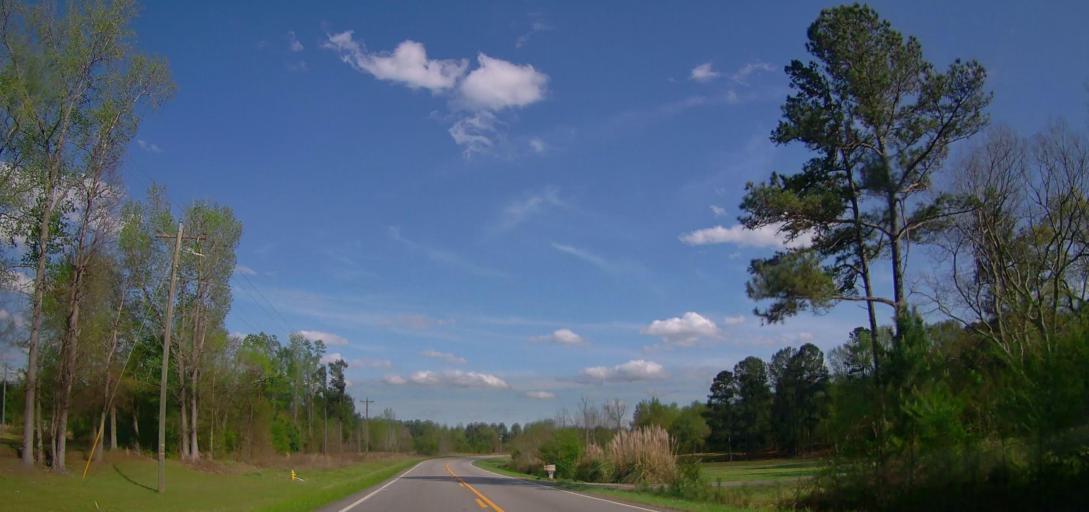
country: US
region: Georgia
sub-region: Baldwin County
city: Hardwick
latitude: 33.0788
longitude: -83.1435
